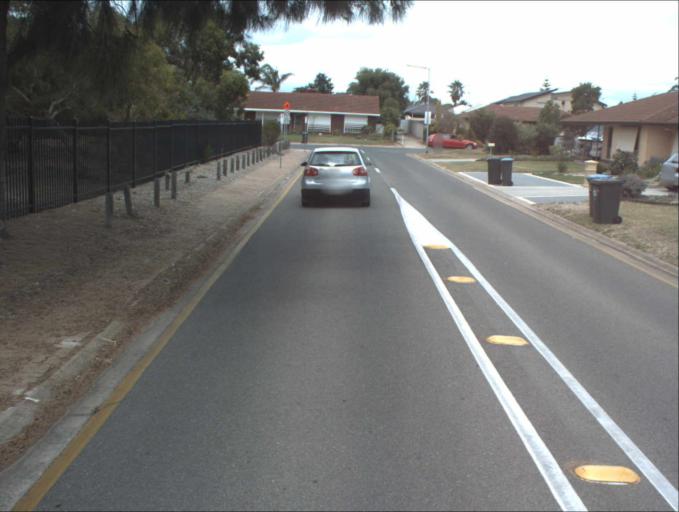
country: AU
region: South Australia
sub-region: Port Adelaide Enfield
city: Birkenhead
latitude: -34.7909
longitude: 138.4967
